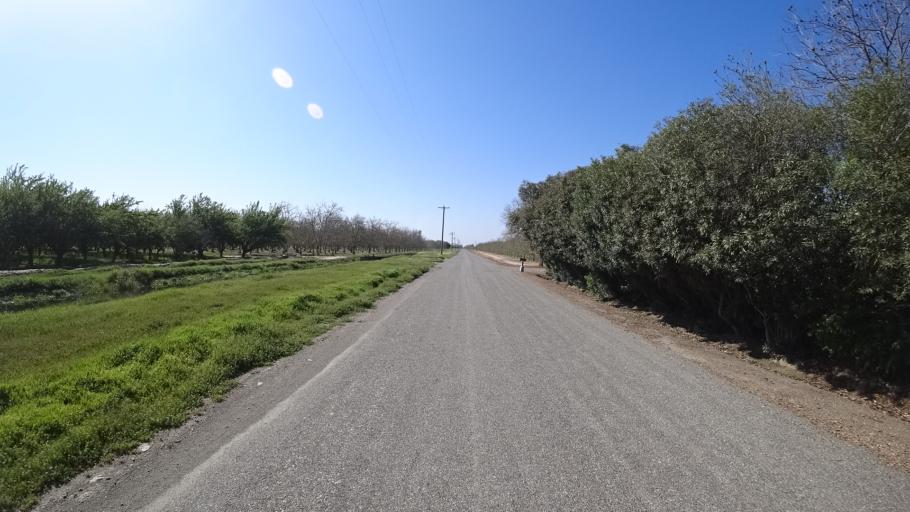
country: US
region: California
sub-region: Glenn County
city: Hamilton City
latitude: 39.6345
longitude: -122.0274
